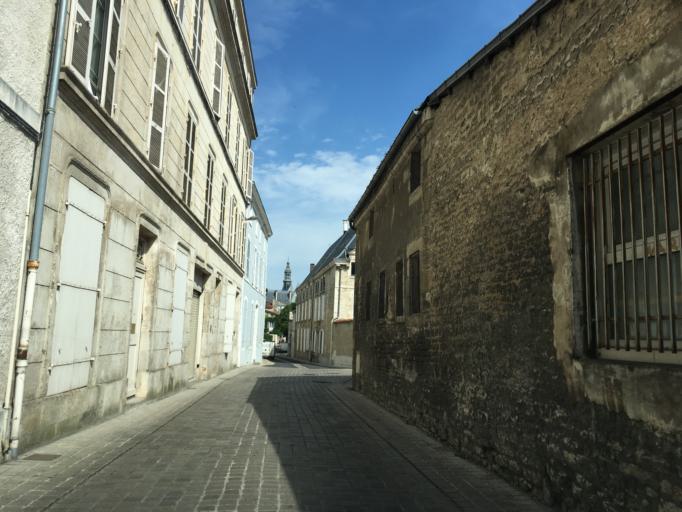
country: FR
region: Poitou-Charentes
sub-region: Departement des Deux-Sevres
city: Niort
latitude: 46.3217
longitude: -0.4618
